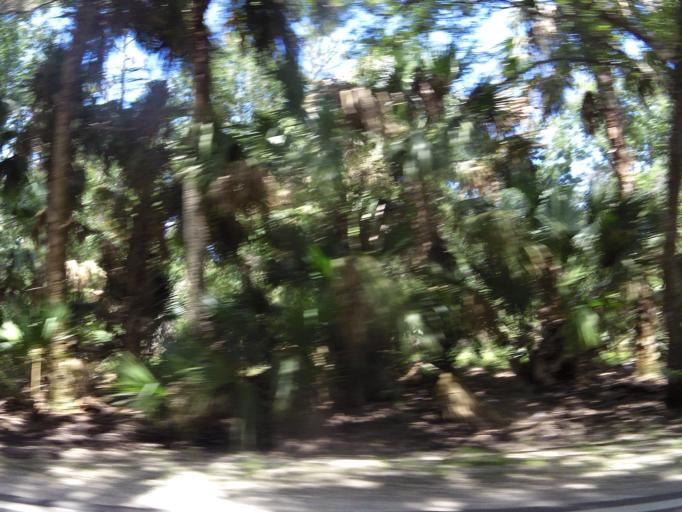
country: US
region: Florida
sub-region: Flagler County
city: Flagler Beach
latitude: 29.3945
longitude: -81.1346
